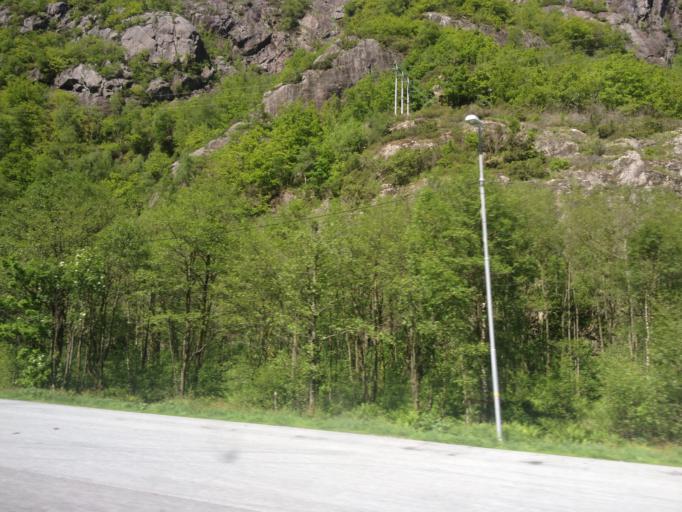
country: NO
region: Rogaland
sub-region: Lund
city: Moi
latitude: 58.4789
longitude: 6.4429
